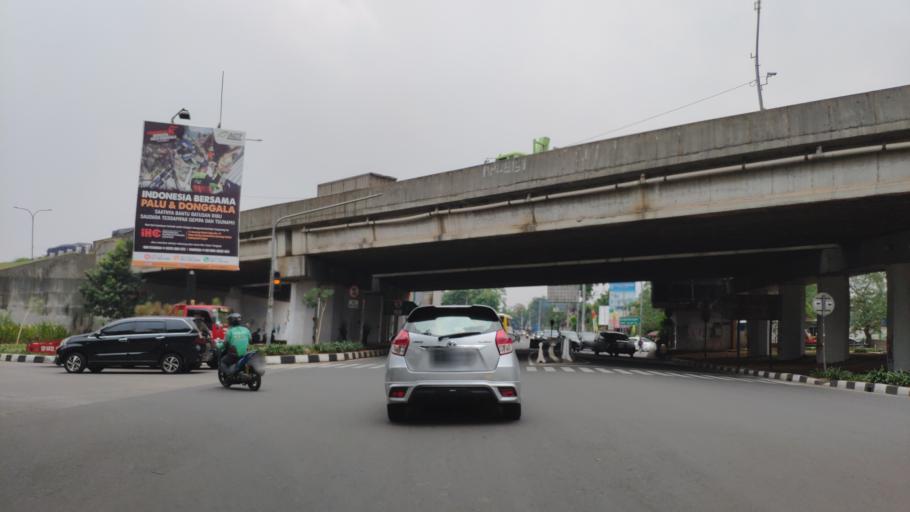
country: ID
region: Banten
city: South Tangerang
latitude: -6.2620
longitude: 106.7668
